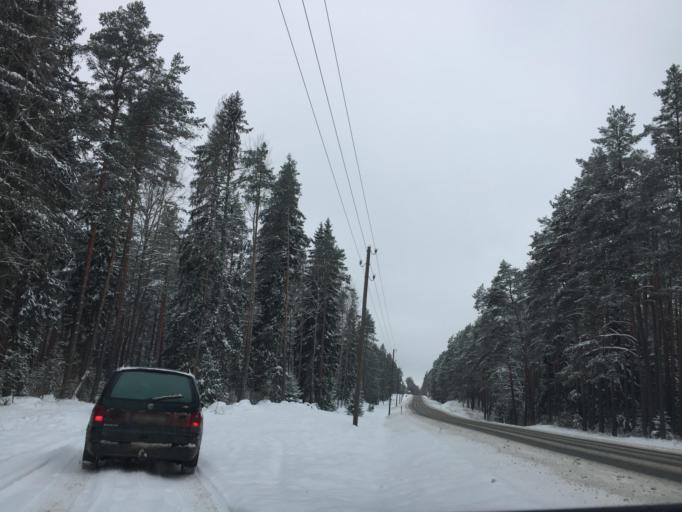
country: LV
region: Smiltene
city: Smiltene
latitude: 57.4047
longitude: 25.9497
